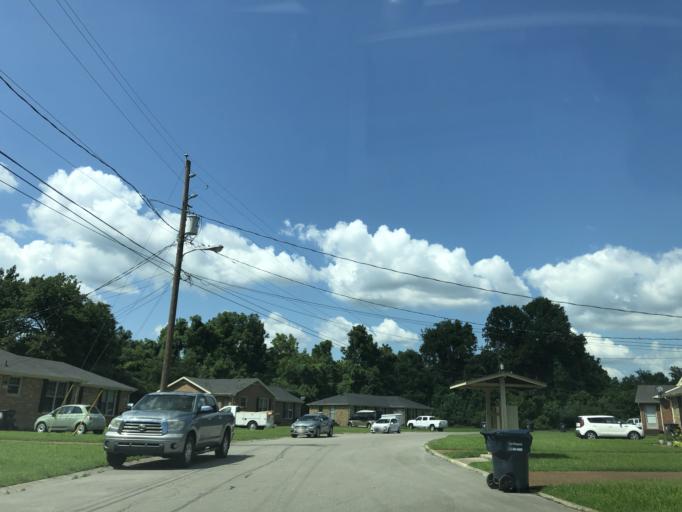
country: US
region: Tennessee
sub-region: Wilson County
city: Green Hill
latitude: 36.2129
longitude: -86.5901
